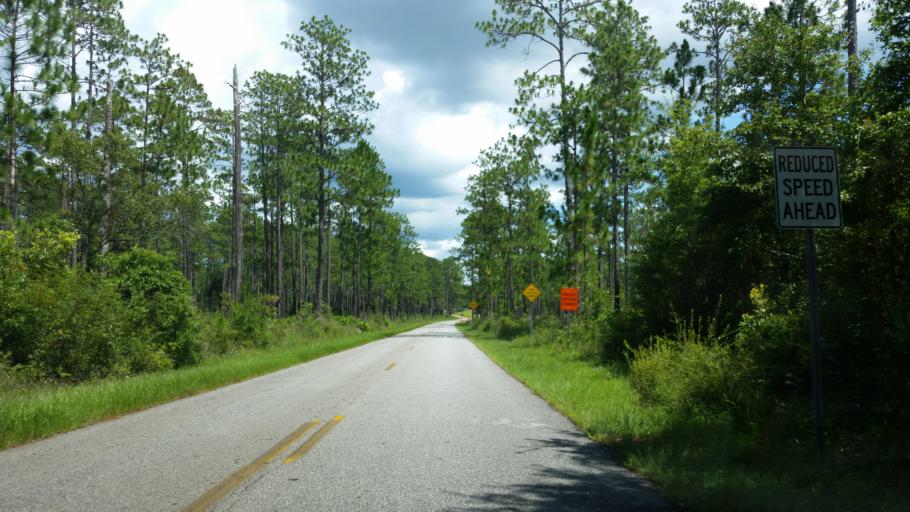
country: US
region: Florida
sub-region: Okaloosa County
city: Crestview
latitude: 30.7270
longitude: -86.7982
